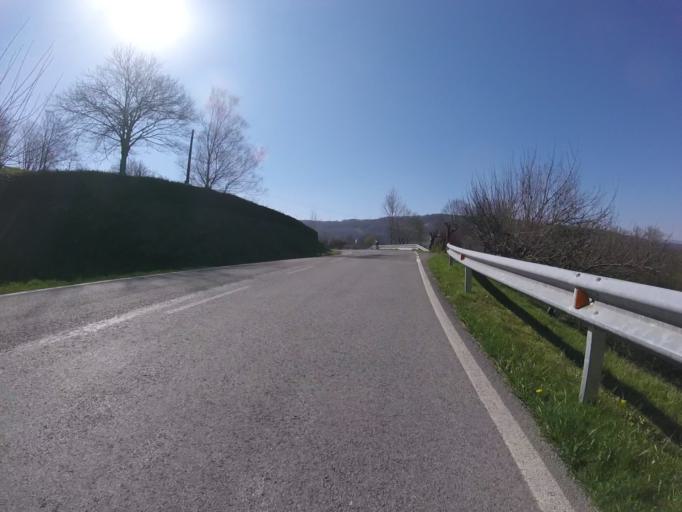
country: ES
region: Navarre
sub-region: Provincia de Navarra
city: Leitza
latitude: 43.0871
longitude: -1.8854
